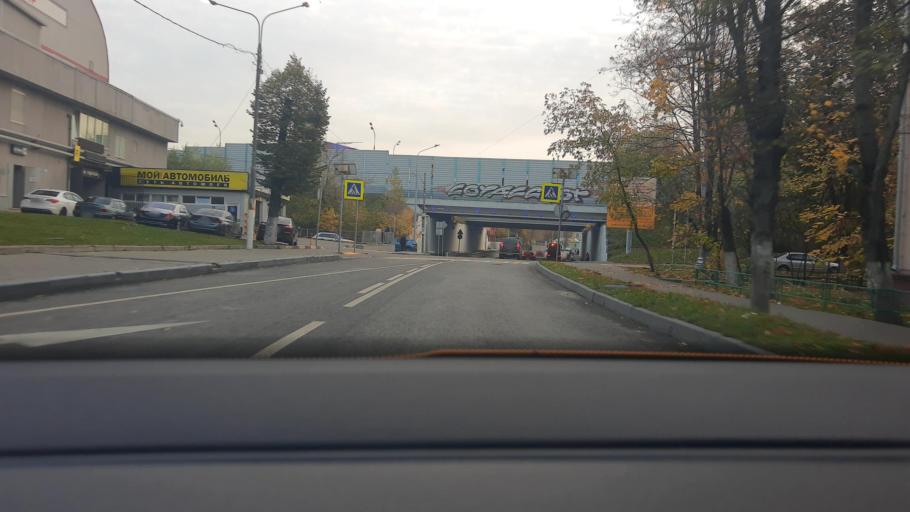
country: RU
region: Moscow
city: Khimki
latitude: 55.8838
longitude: 37.4536
